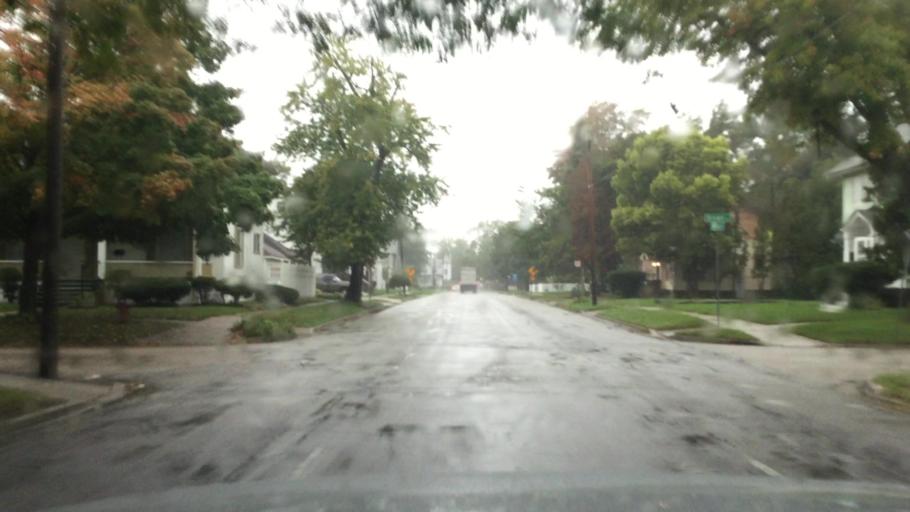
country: US
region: Michigan
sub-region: Saginaw County
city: Saginaw
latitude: 43.4166
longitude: -83.9383
